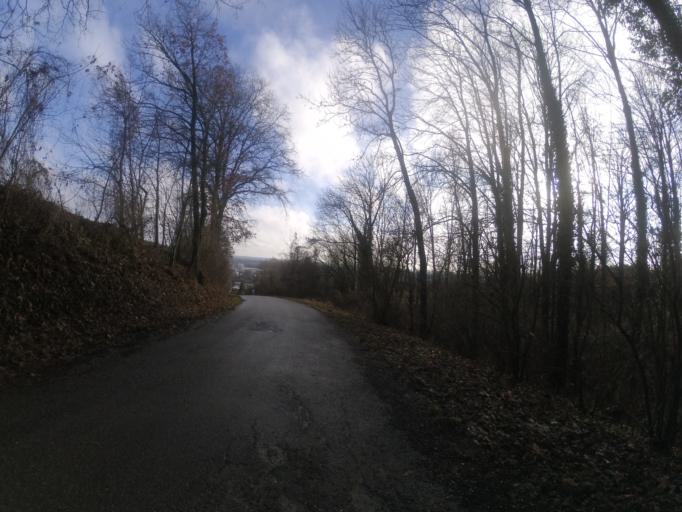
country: DE
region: Bavaria
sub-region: Swabia
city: Neu-Ulm
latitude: 48.4398
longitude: 10.0438
